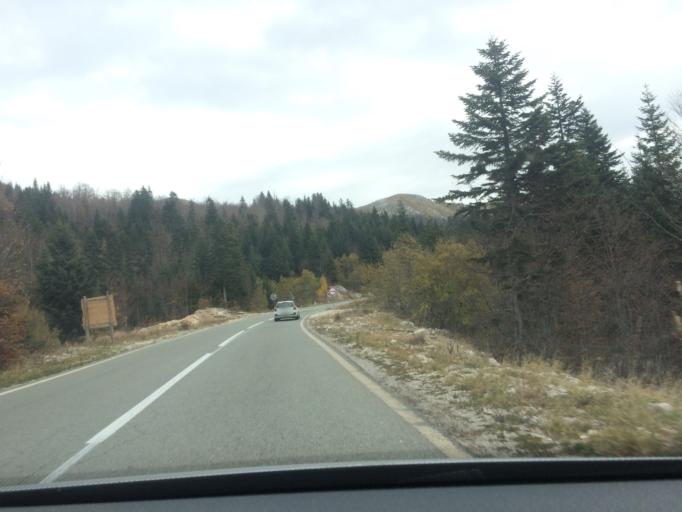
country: ME
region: Opstina Savnik
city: Savnik
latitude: 42.9004
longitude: 19.0475
